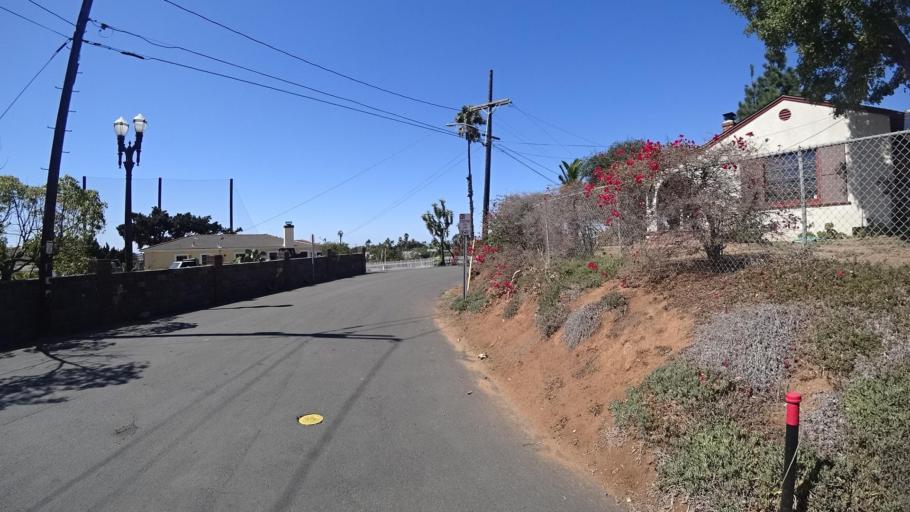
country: US
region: California
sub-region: San Diego County
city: National City
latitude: 32.6629
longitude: -117.0832
